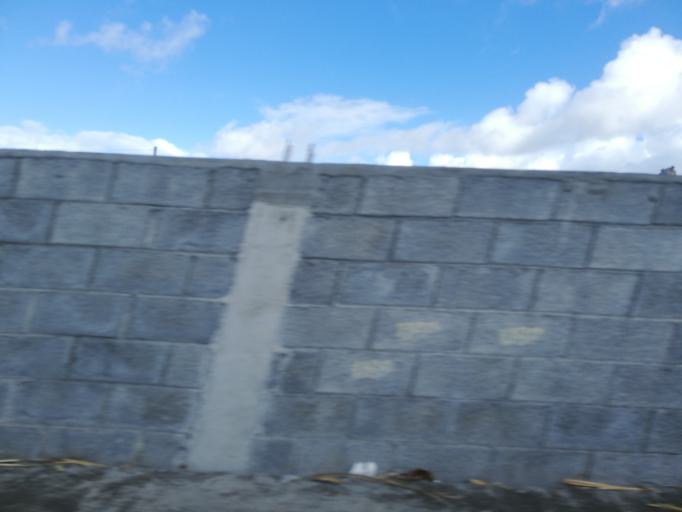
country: MU
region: Flacq
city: Bel Air Riviere Seche
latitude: -20.2636
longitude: 57.7408
